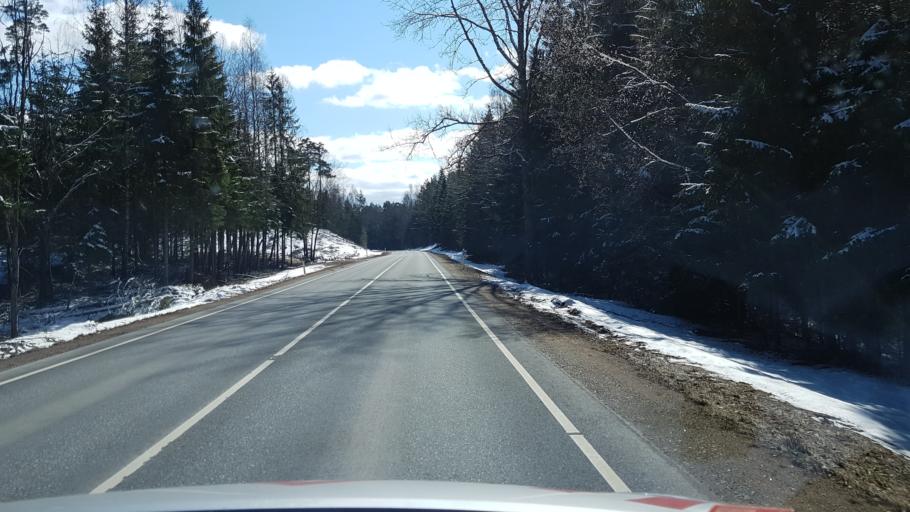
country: EE
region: Laeaene-Virumaa
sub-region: Tapa vald
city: Tapa
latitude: 59.4081
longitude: 26.0024
